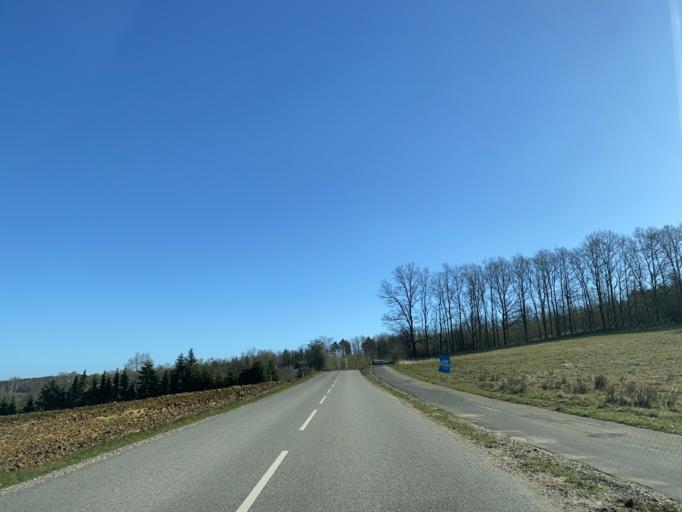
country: DK
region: Central Jutland
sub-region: Favrskov Kommune
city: Ulstrup
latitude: 56.3803
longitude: 9.7418
